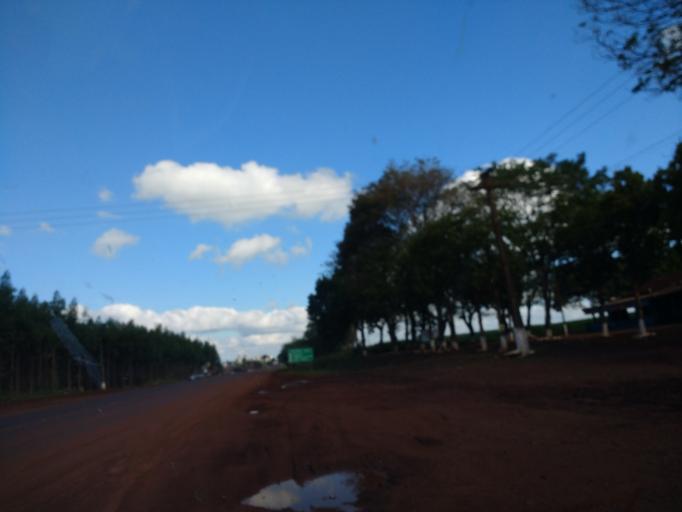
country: BR
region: Parana
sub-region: Palotina
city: Palotina
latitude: -24.3971
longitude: -53.5378
